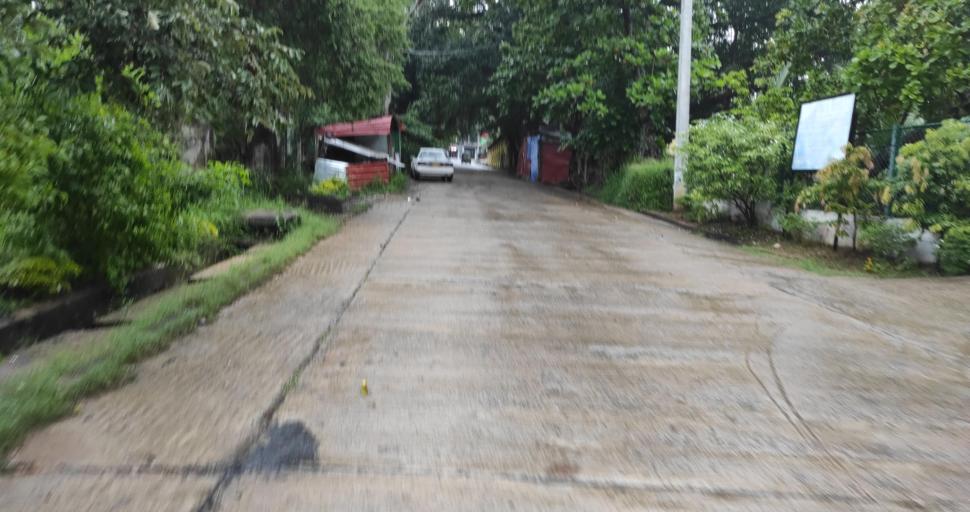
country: LK
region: Eastern Province
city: Trincomalee
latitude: 8.3657
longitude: 81.0038
